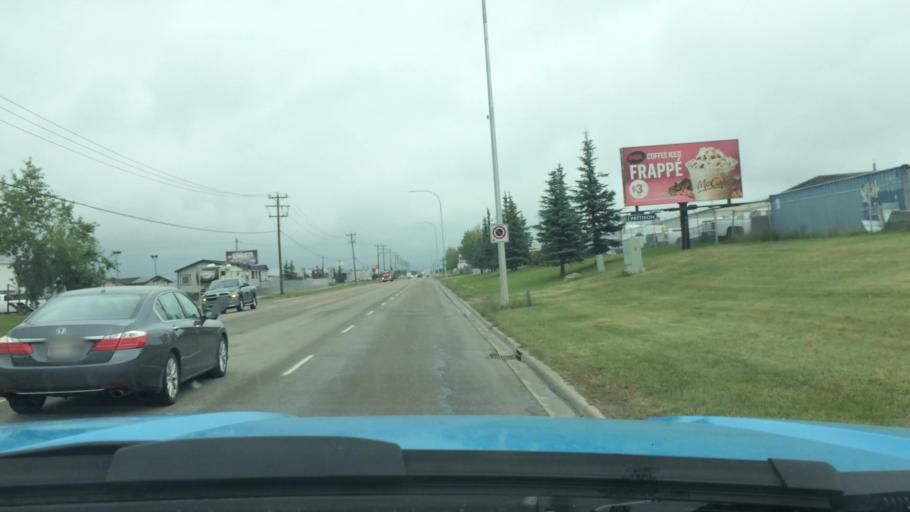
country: CA
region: Alberta
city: Airdrie
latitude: 51.2933
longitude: -113.9899
